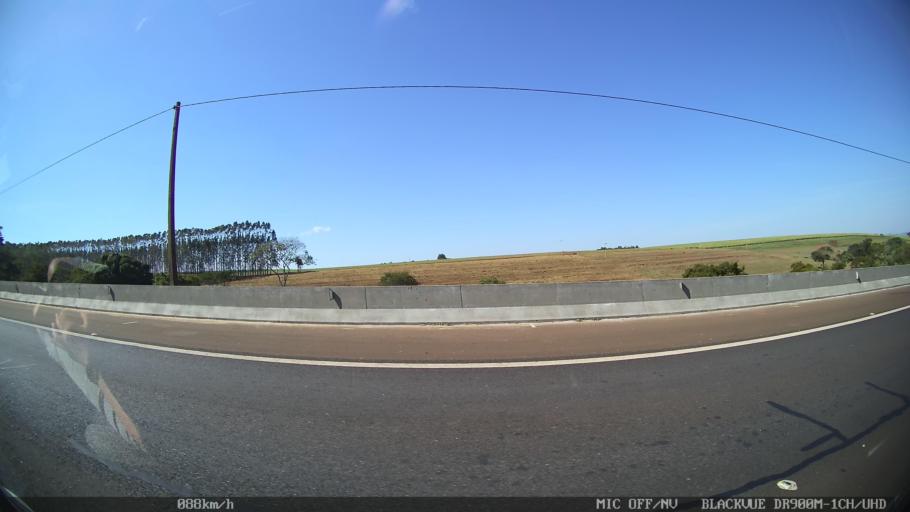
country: BR
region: Sao Paulo
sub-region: Franca
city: Franca
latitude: -20.6954
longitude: -47.4993
